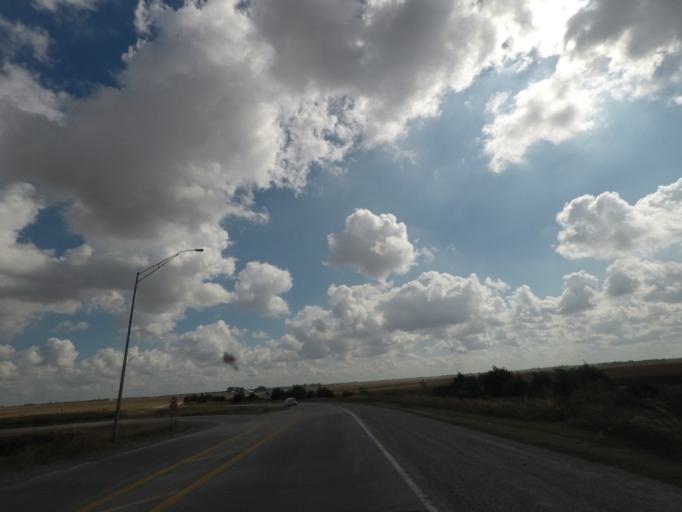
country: US
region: Iowa
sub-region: Story County
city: Nevada
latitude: 42.0065
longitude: -93.4341
